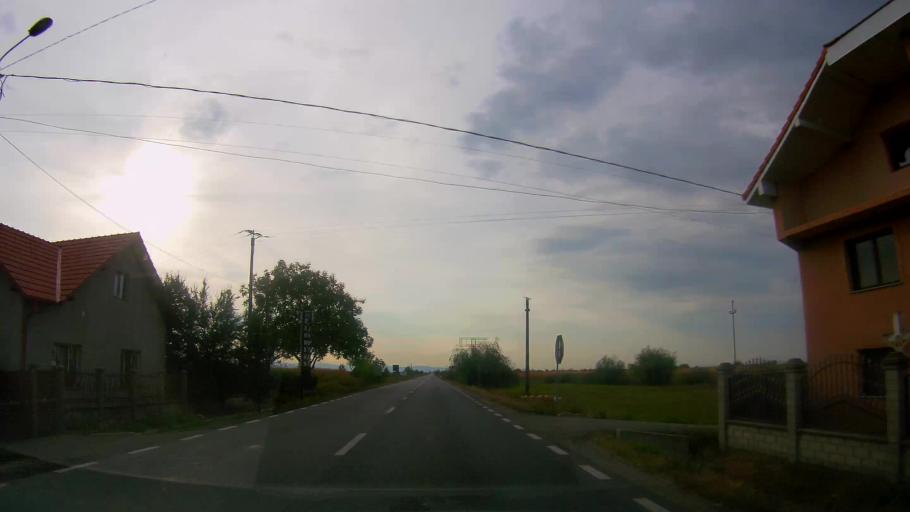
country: RO
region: Satu Mare
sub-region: Comuna Halmeu
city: Halmeu
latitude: 47.9701
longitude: 23.0358
